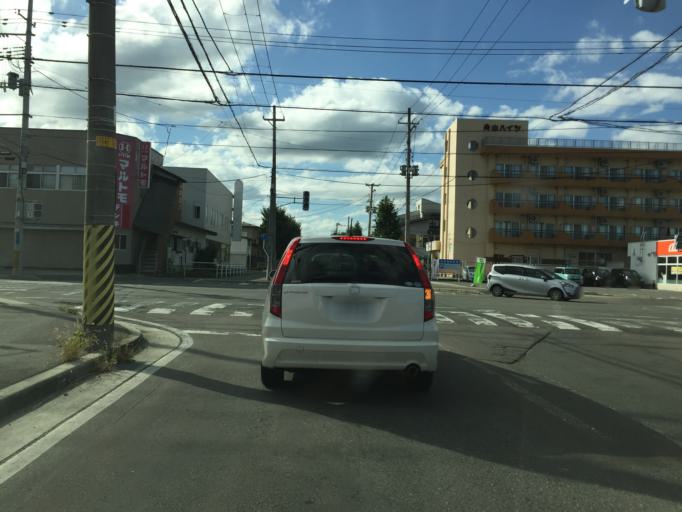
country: JP
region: Yamagata
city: Yonezawa
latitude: 37.9181
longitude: 140.1148
